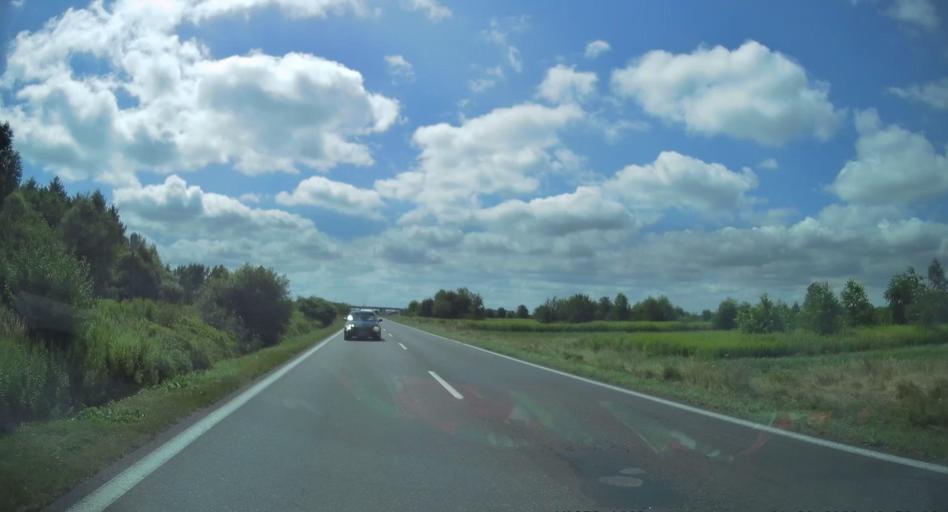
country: PL
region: Subcarpathian Voivodeship
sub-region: Powiat mielecki
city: Padew Narodowa
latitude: 50.3890
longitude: 21.4616
